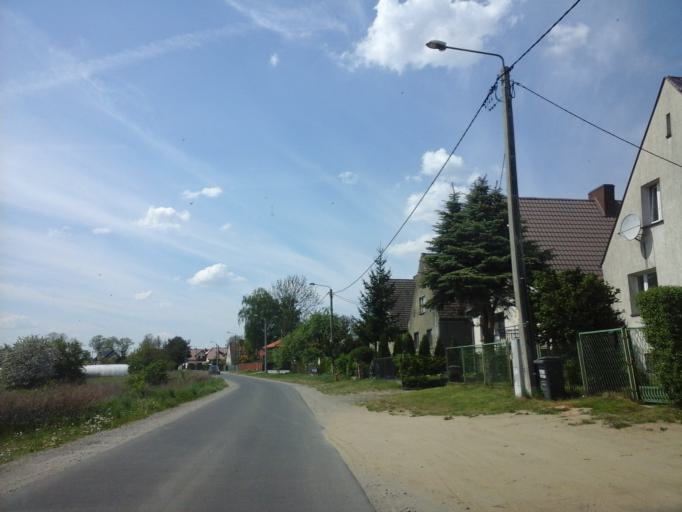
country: PL
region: West Pomeranian Voivodeship
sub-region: Powiat choszczenski
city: Choszczno
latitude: 53.1802
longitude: 15.4291
